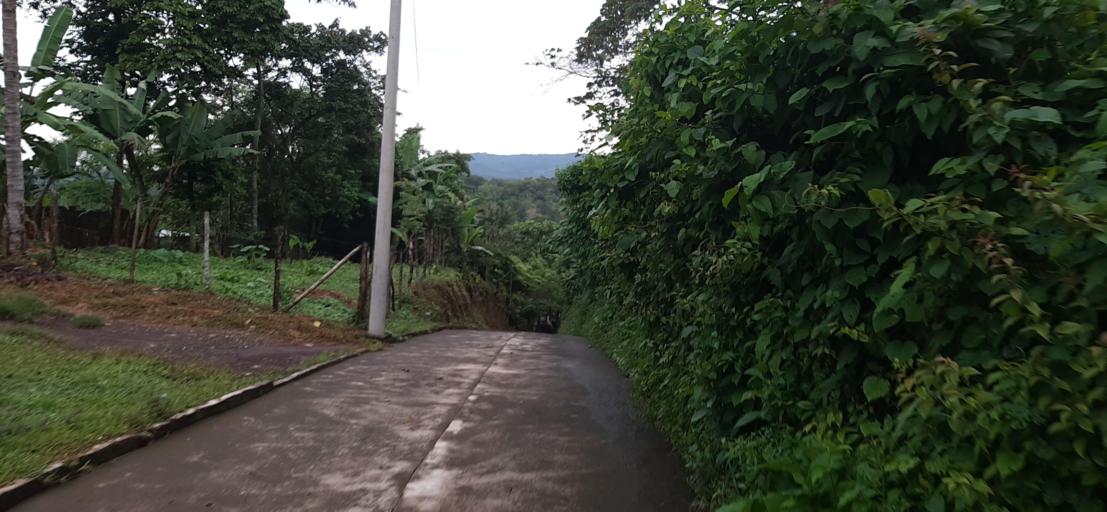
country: GT
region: Retalhuleu
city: San Felipe
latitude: 14.6280
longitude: -91.5982
